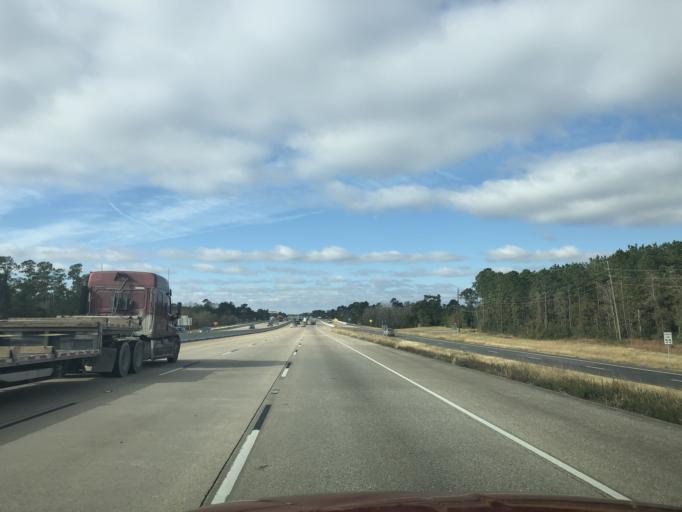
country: US
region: Texas
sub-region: Chambers County
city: Anahuac
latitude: 29.8405
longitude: -94.6487
